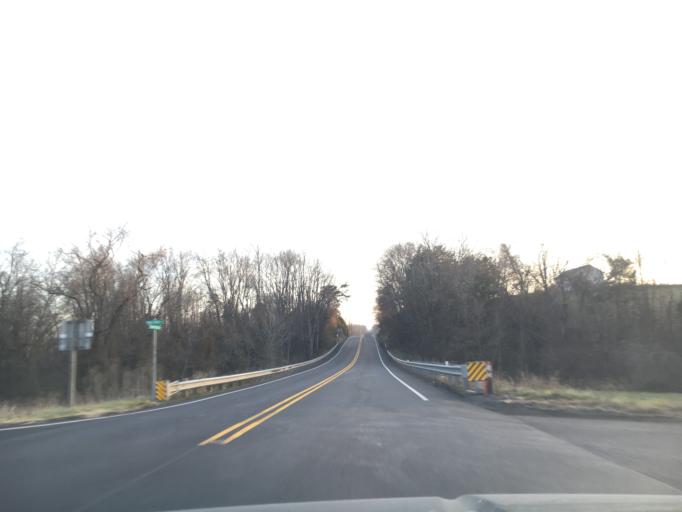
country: US
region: Virginia
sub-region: Culpeper County
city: Culpeper
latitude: 38.3175
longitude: -77.9560
